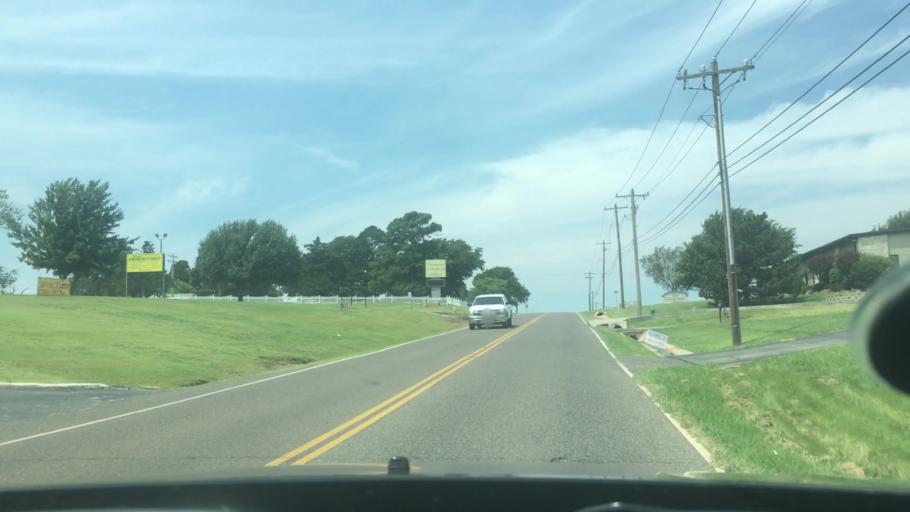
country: US
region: Oklahoma
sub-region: Pottawatomie County
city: Shawnee
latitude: 35.3617
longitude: -96.9082
